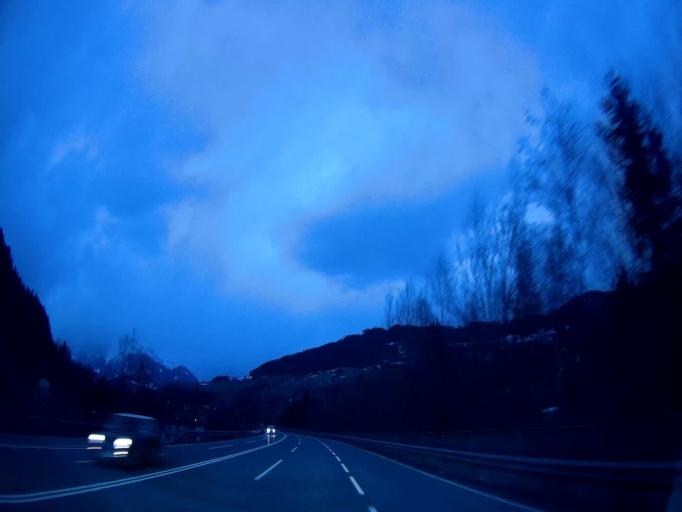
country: AT
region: Salzburg
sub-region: Politischer Bezirk Sankt Johann im Pongau
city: Bischofshofen
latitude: 47.3888
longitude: 13.2186
